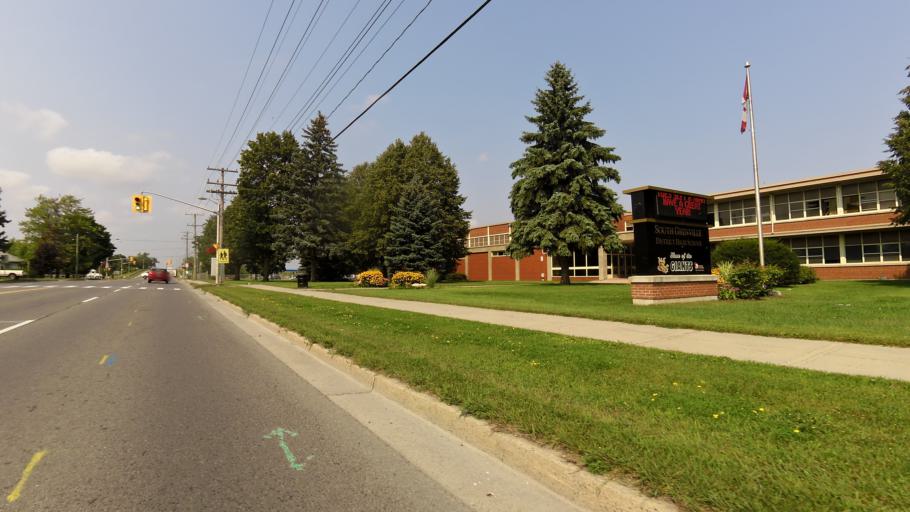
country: CA
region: Ontario
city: Prescott
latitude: 44.7195
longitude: -75.5222
